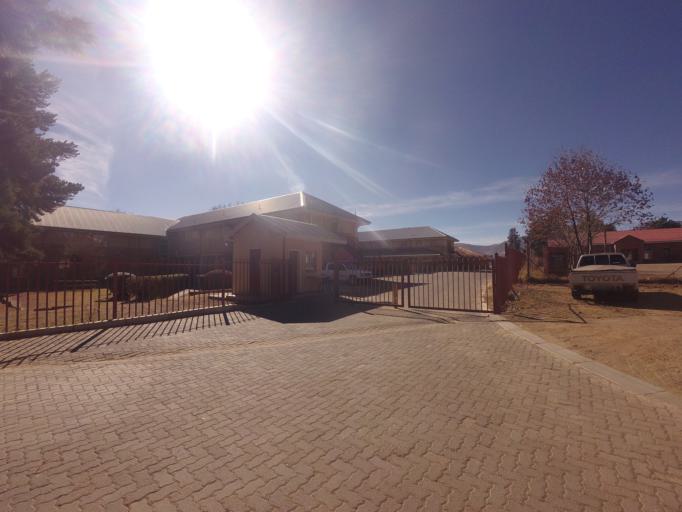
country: LS
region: Maseru
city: Nako
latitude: -29.4481
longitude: 27.7248
